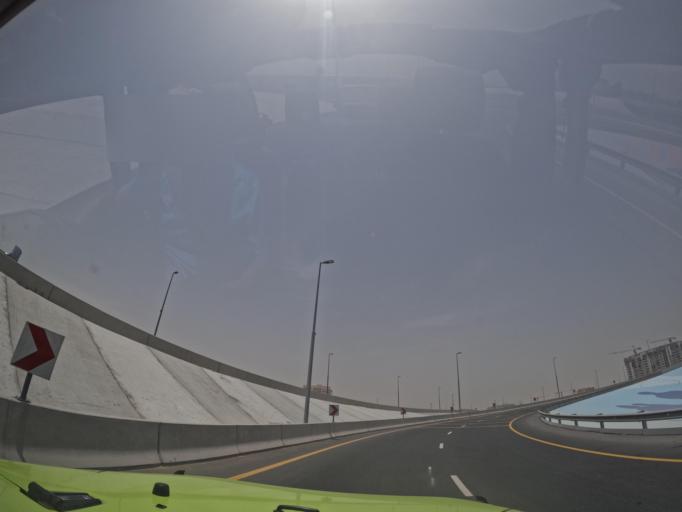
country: AE
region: Dubai
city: Dubai
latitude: 25.1026
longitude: 55.3786
